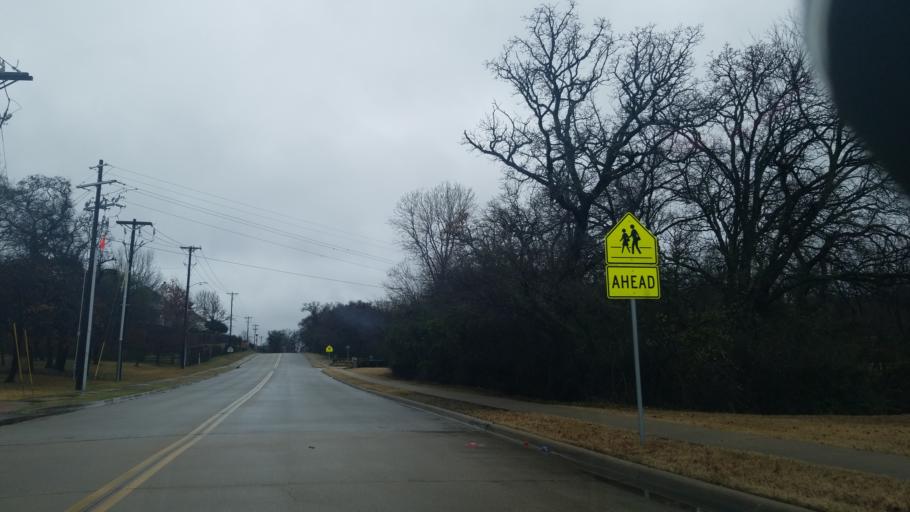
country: US
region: Texas
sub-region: Denton County
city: Corinth
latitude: 33.1465
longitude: -97.0854
